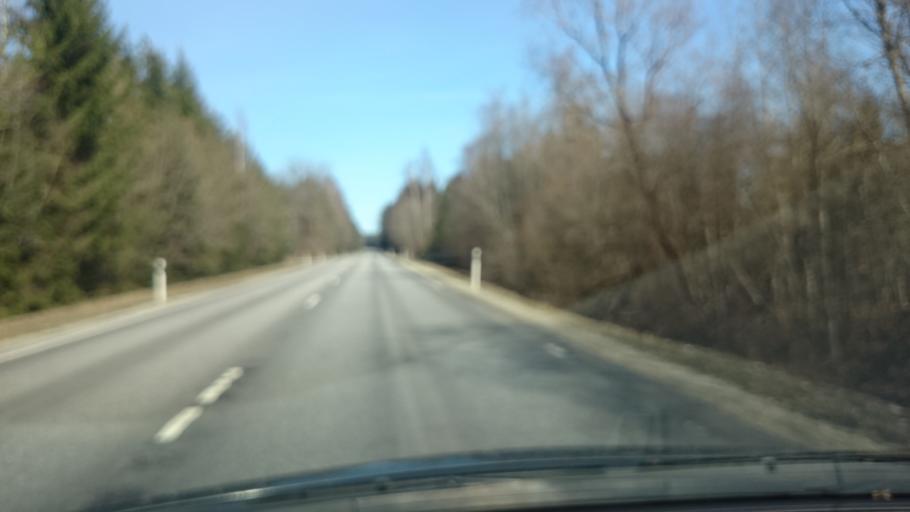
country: EE
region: Jaervamaa
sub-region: Tueri vald
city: Sarevere
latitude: 58.6907
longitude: 25.2471
